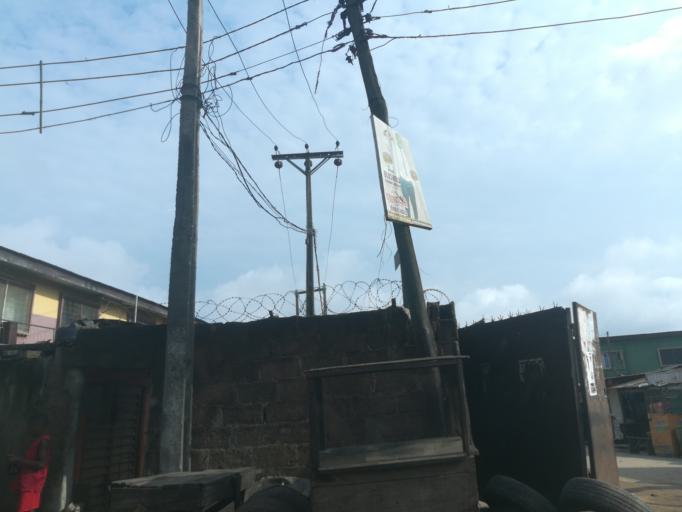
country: NG
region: Lagos
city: Agege
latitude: 6.6177
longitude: 3.3136
